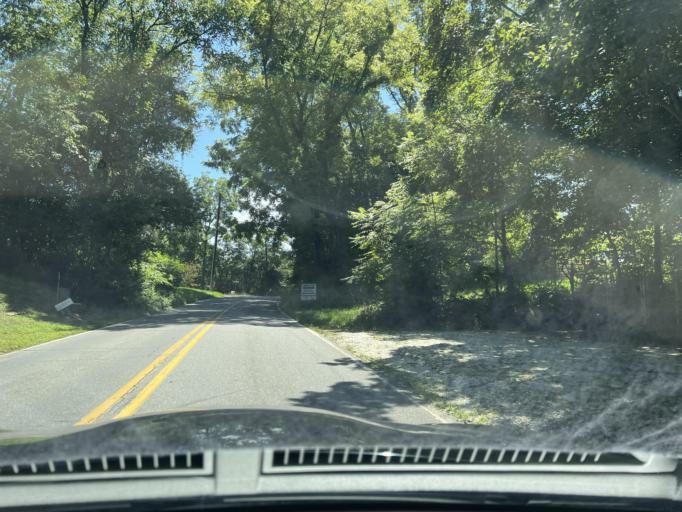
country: US
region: North Carolina
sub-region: Buncombe County
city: Fairview
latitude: 35.5166
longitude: -82.3994
